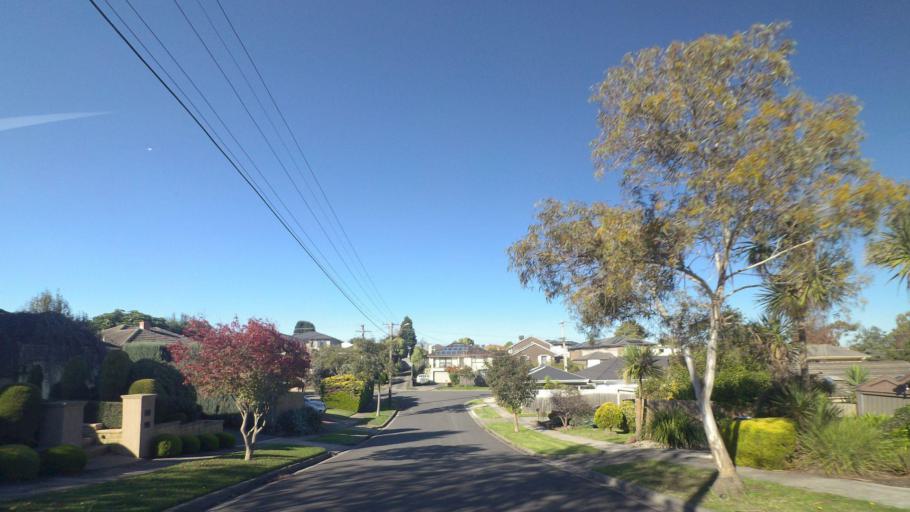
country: AU
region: Victoria
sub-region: Manningham
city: Doncaster East
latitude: -37.7935
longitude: 145.1535
